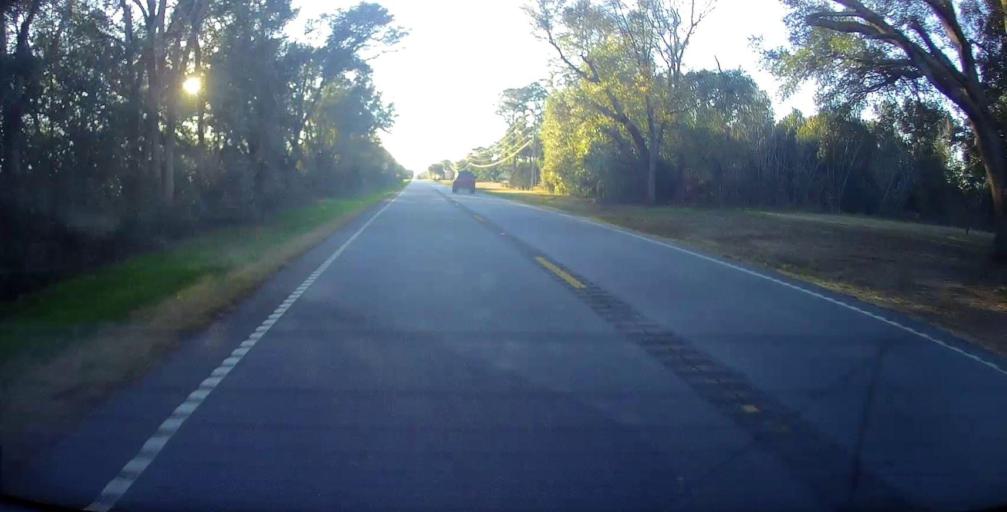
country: US
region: Georgia
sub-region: Dougherty County
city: Albany
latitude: 31.5041
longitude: -84.2370
